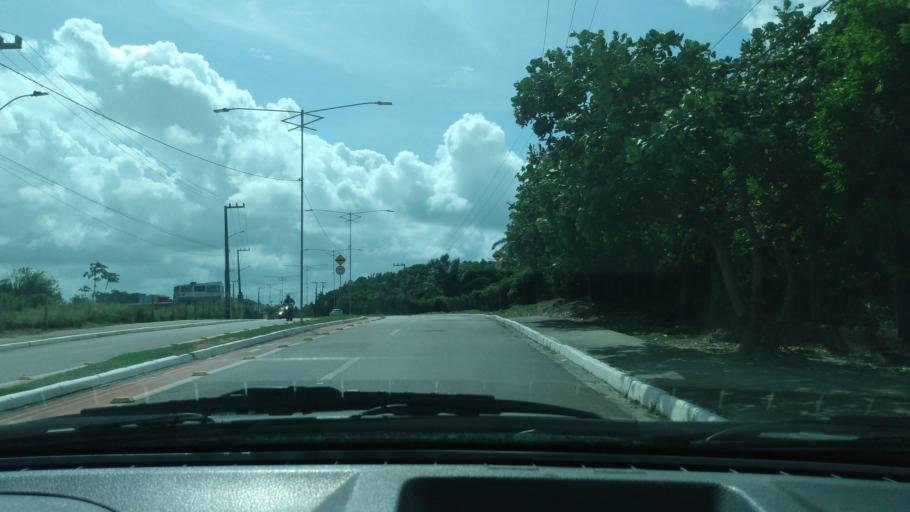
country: BR
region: Pernambuco
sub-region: Cabo De Santo Agostinho
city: Cabo
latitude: -8.3060
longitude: -34.9465
